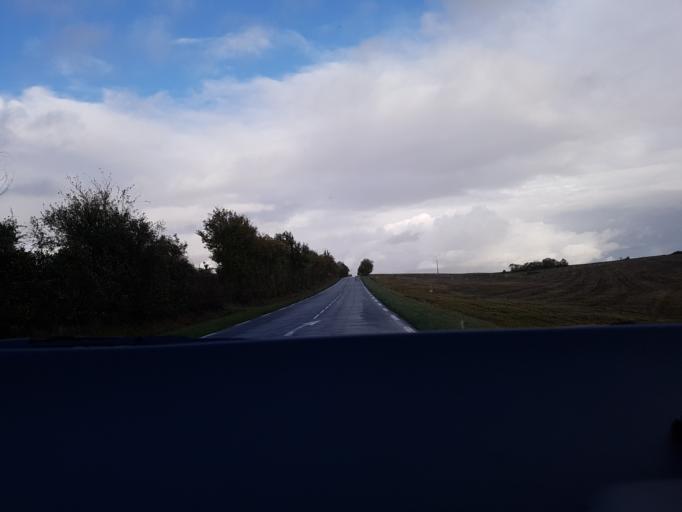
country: FR
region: Poitou-Charentes
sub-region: Departement de la Charente-Maritime
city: Aulnay
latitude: 46.0087
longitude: -0.3797
